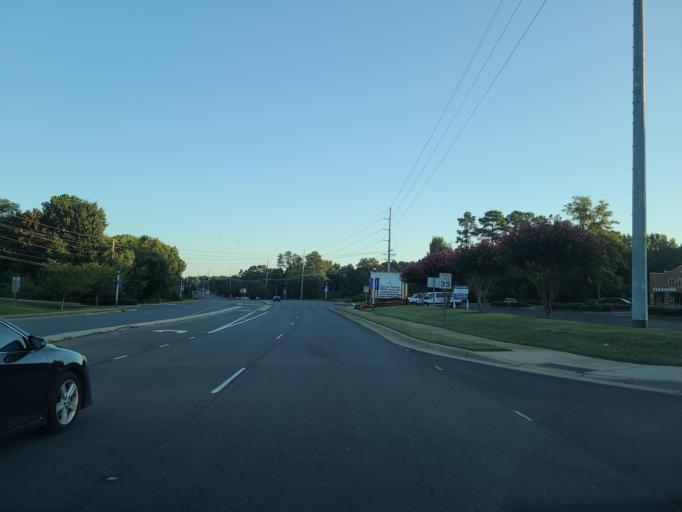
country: US
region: North Carolina
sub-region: Union County
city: Weddington
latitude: 35.0233
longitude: -80.7625
